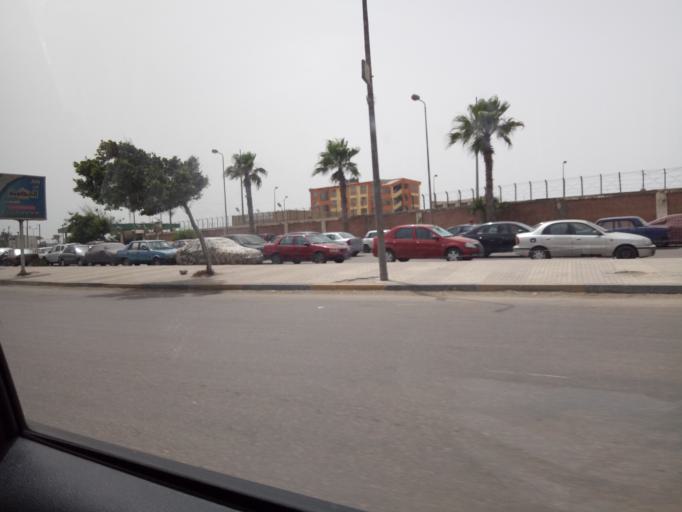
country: EG
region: Alexandria
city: Alexandria
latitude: 31.1455
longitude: 29.8380
